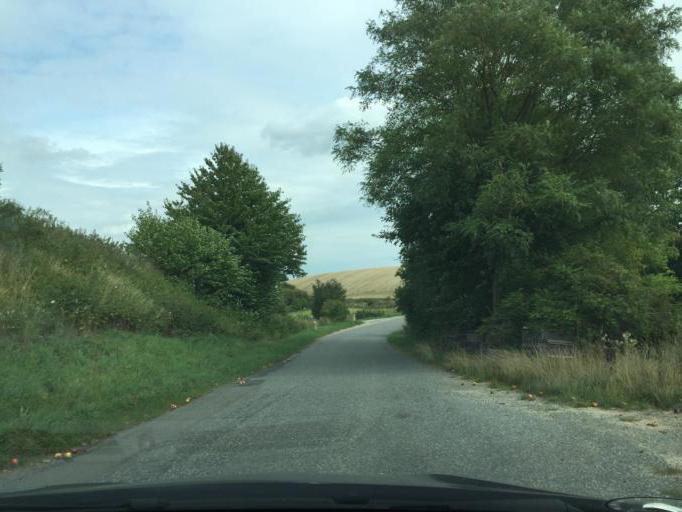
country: DK
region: South Denmark
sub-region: Assens Kommune
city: Vissenbjerg
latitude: 55.3534
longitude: 10.1154
